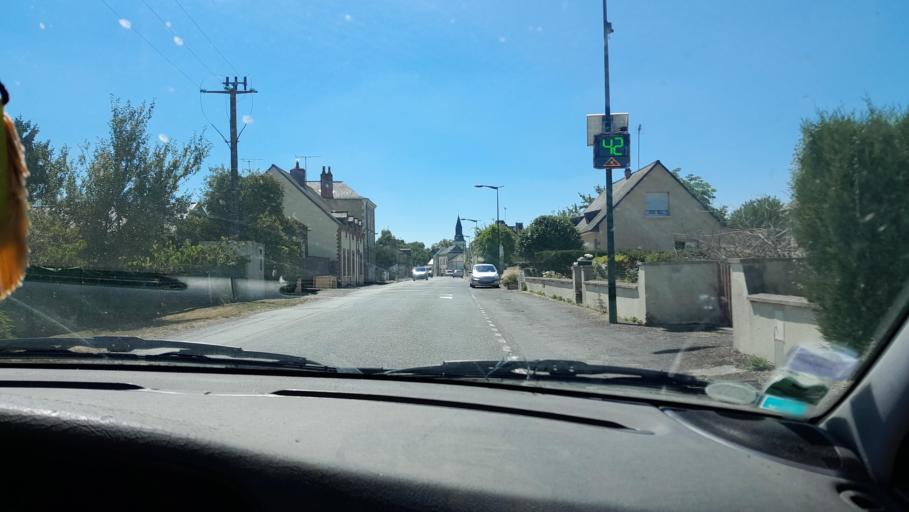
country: FR
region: Pays de la Loire
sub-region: Departement de la Mayenne
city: Ballots
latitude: 47.9435
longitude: -1.0819
